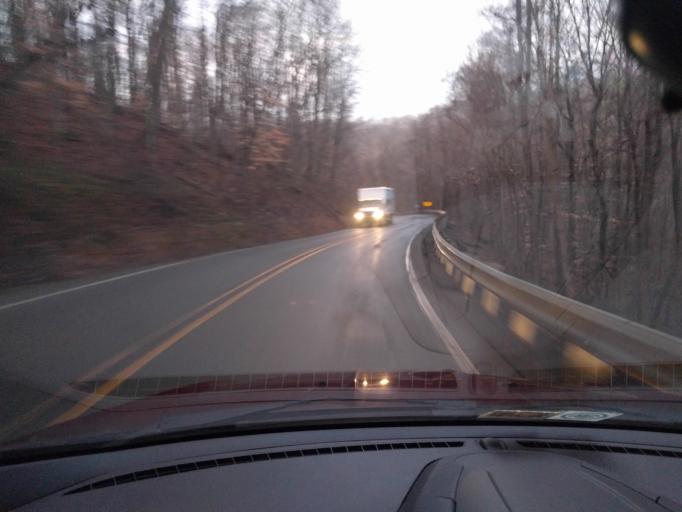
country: US
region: West Virginia
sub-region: Greenbrier County
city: Rainelle
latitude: 37.9889
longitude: -80.8576
